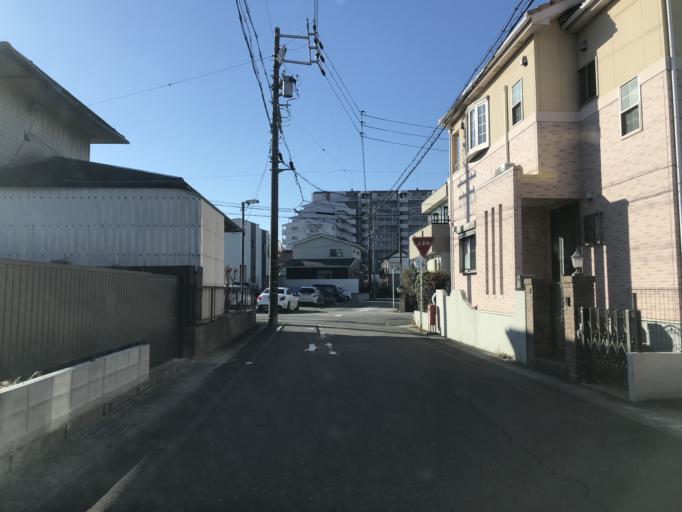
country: JP
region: Aichi
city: Nagoya-shi
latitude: 35.2034
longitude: 136.8727
